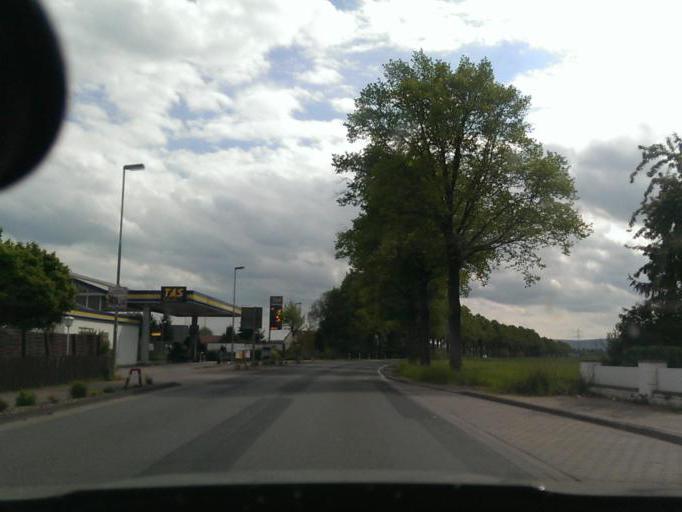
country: DE
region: Lower Saxony
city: Elze
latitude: 52.1507
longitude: 9.7383
